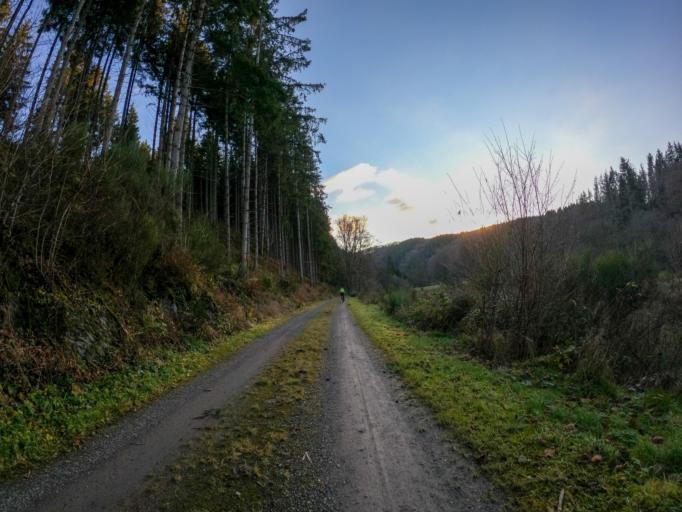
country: LU
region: Diekirch
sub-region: Canton de Wiltz
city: Bavigne
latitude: 49.9464
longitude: 5.8362
